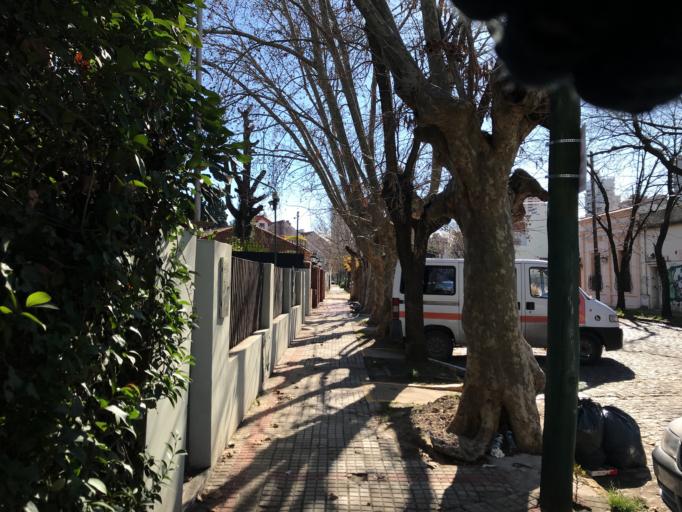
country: AR
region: Buenos Aires
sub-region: Partido de Lomas de Zamora
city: Lomas de Zamora
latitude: -34.7697
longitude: -58.4003
